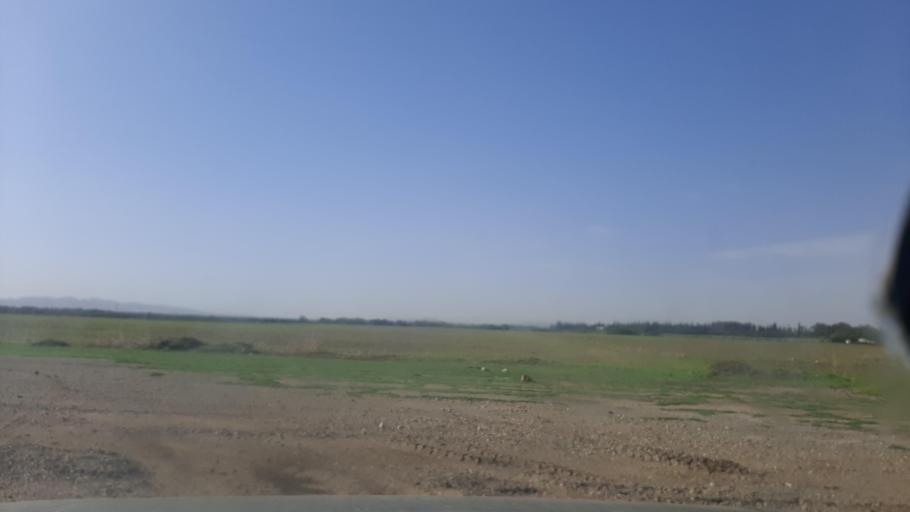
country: TN
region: Tunis
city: La Mohammedia
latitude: 36.6427
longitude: 10.0904
